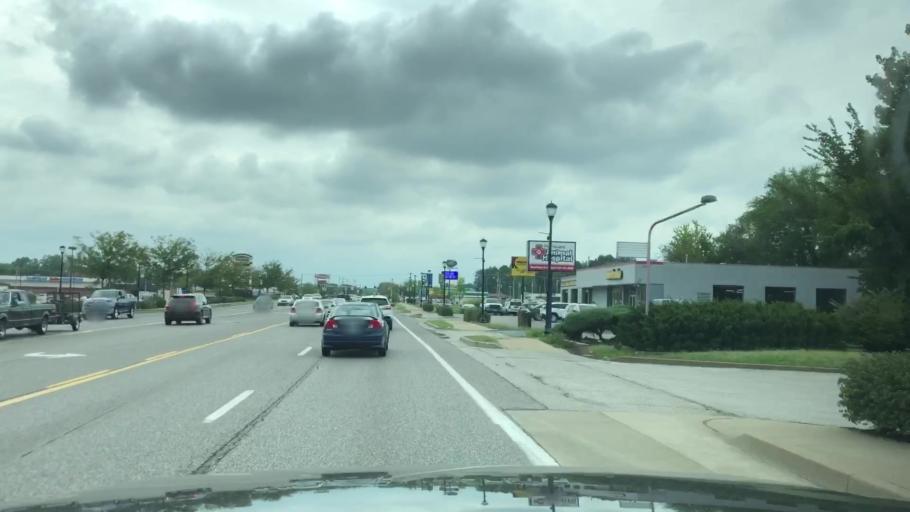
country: US
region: Missouri
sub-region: Saint Louis County
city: Florissant
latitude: 38.7989
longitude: -90.3369
